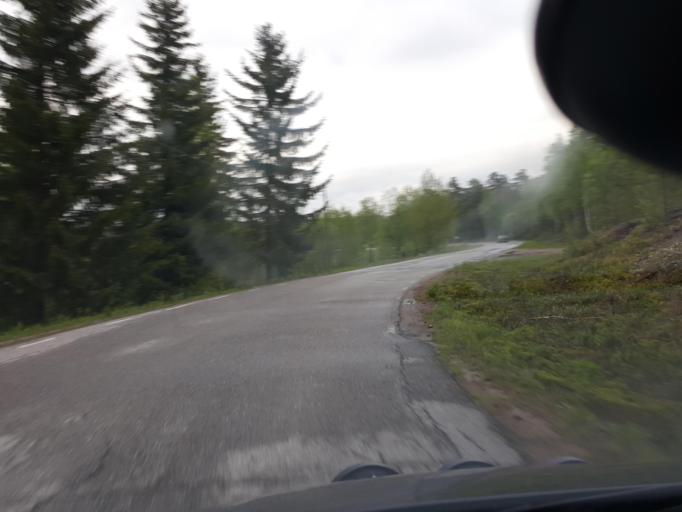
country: SE
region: Gaevleborg
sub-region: Ljusdals Kommun
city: Jaervsoe
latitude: 61.7504
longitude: 16.1926
